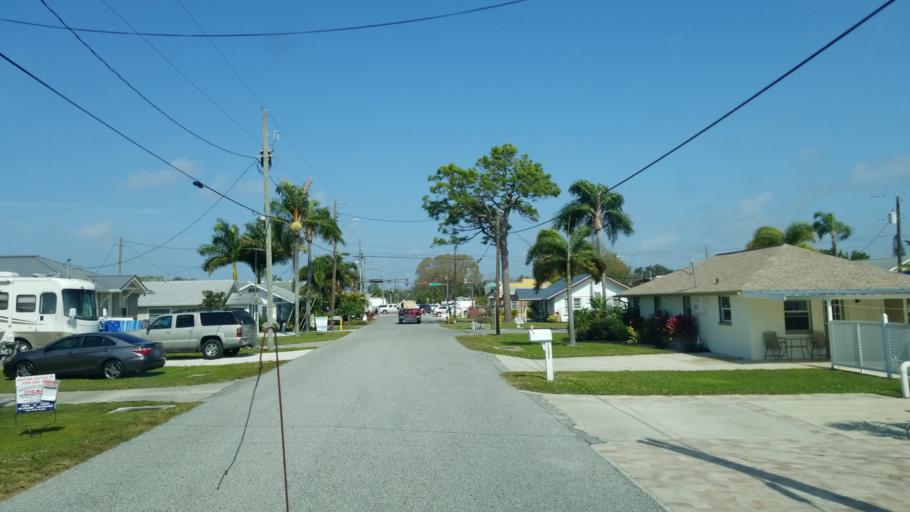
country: US
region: Florida
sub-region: Sarasota County
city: Southgate
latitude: 27.3216
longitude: -82.5017
